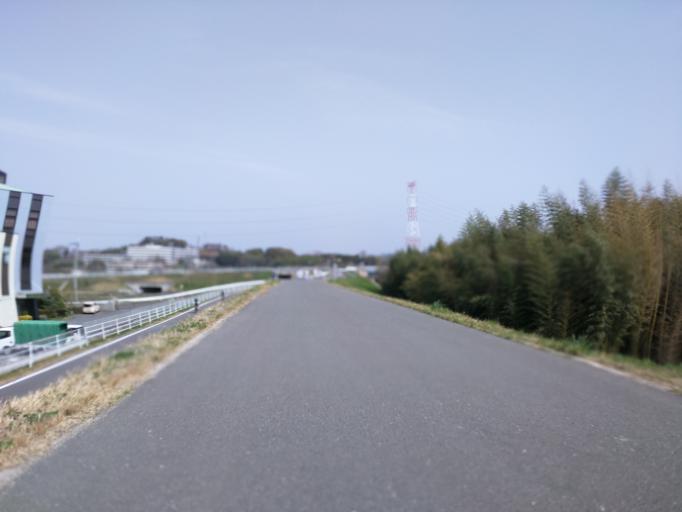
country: JP
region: Kyoto
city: Tanabe
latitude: 34.7974
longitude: 135.7947
